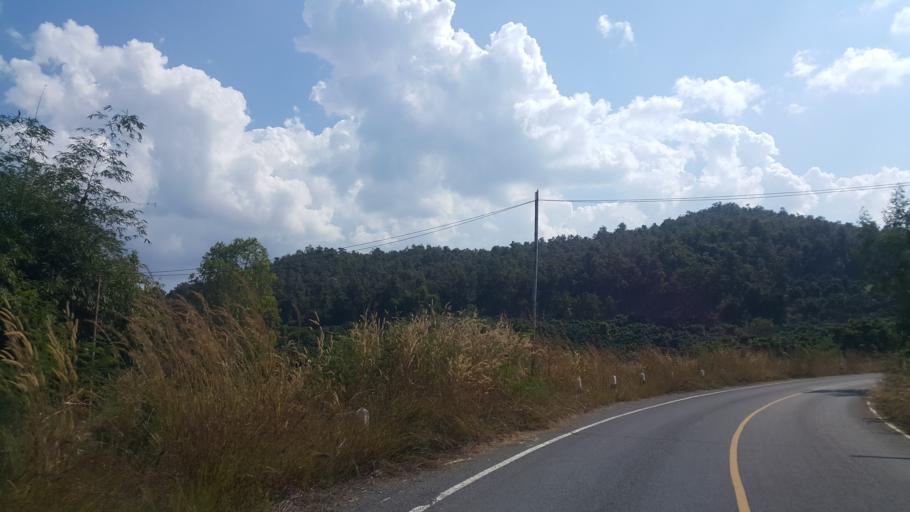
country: TH
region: Lamphun
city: Ban Thi
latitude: 18.6349
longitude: 99.1615
